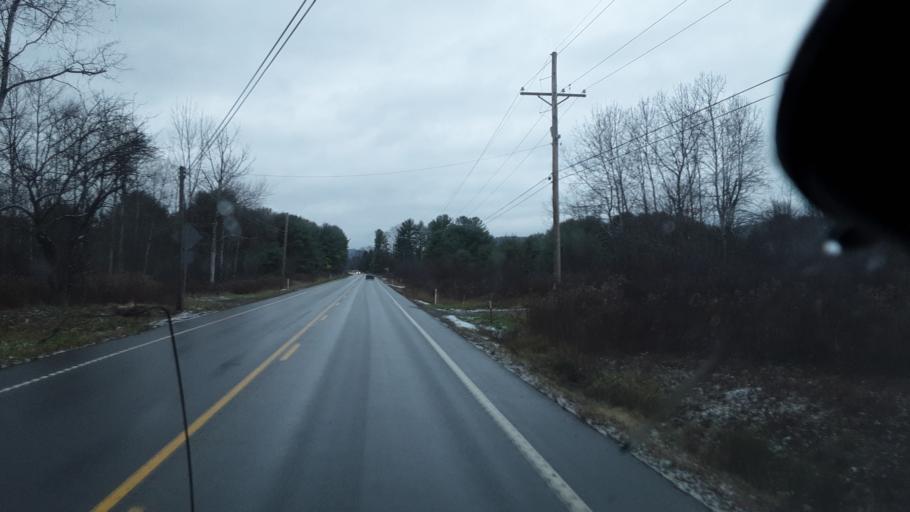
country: US
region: Pennsylvania
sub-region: Potter County
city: Shinglehouse
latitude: 41.9363
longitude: -78.1320
